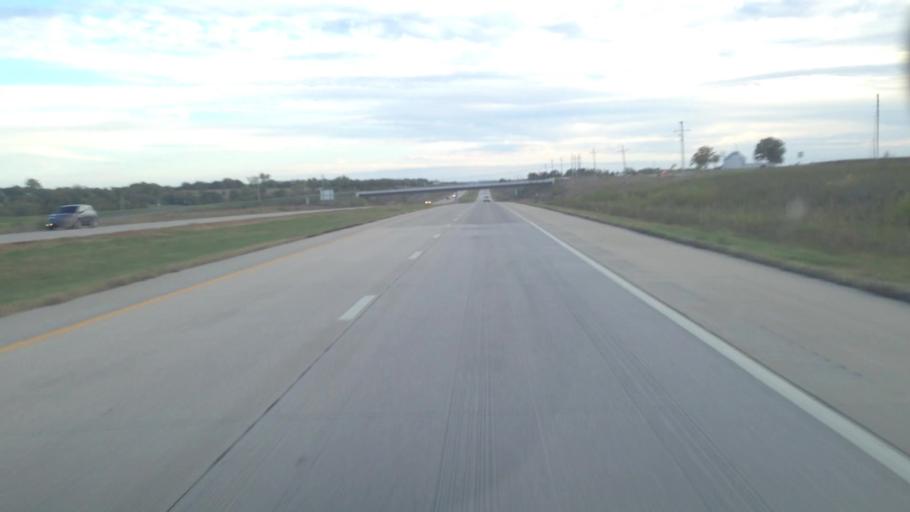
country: US
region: Kansas
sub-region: Douglas County
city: Baldwin City
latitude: 38.8230
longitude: -95.2692
